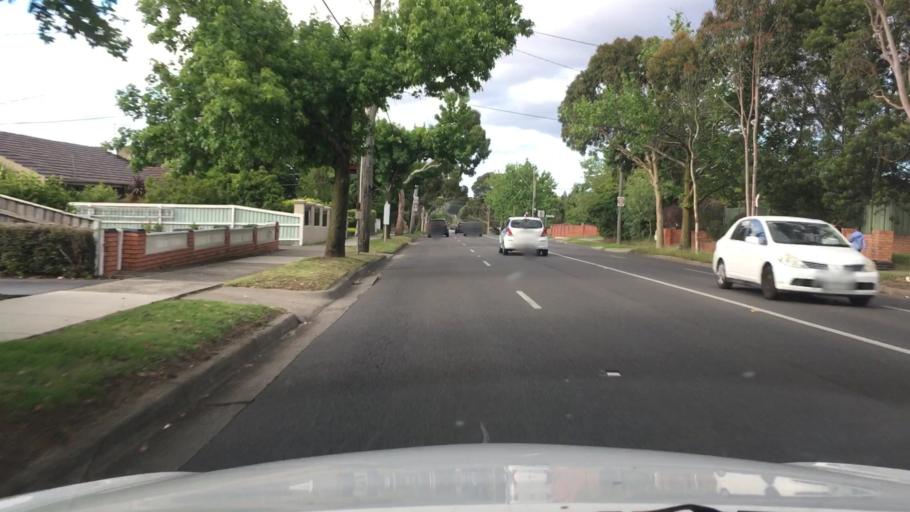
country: AU
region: Victoria
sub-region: Monash
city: Ashwood
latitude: -37.8738
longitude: 145.1293
